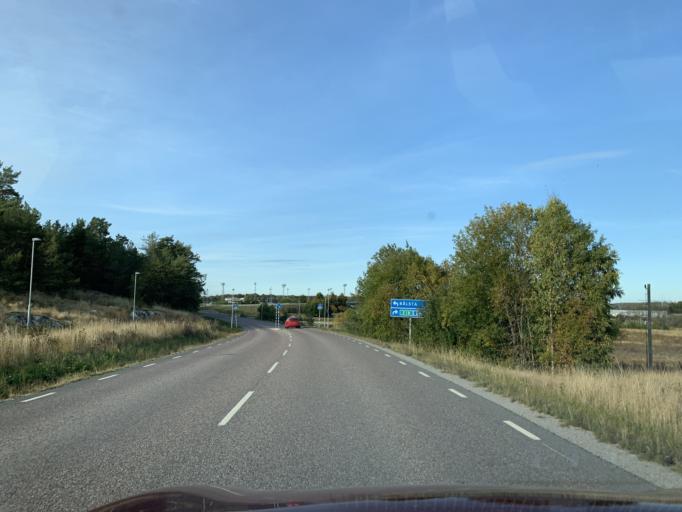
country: SE
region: Stockholm
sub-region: Upplands-Bro Kommun
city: Bro
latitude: 59.5145
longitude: 17.6152
